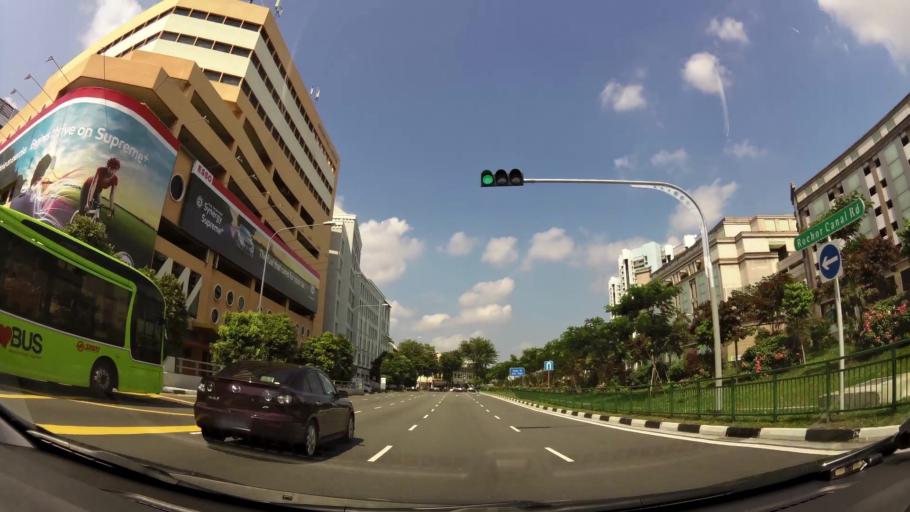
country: SG
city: Singapore
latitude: 1.3041
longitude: 103.8521
